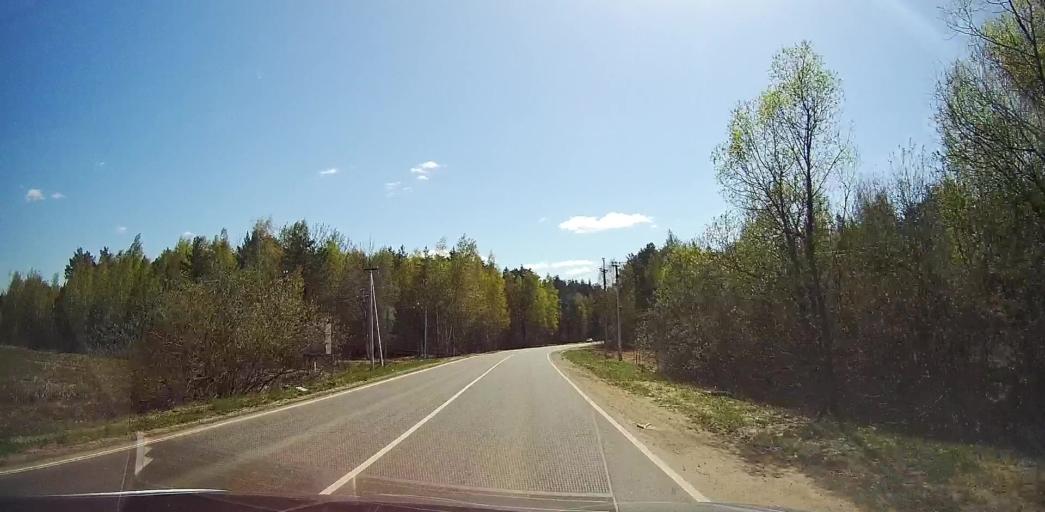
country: RU
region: Moskovskaya
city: Beloozerskiy
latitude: 55.5021
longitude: 38.4309
